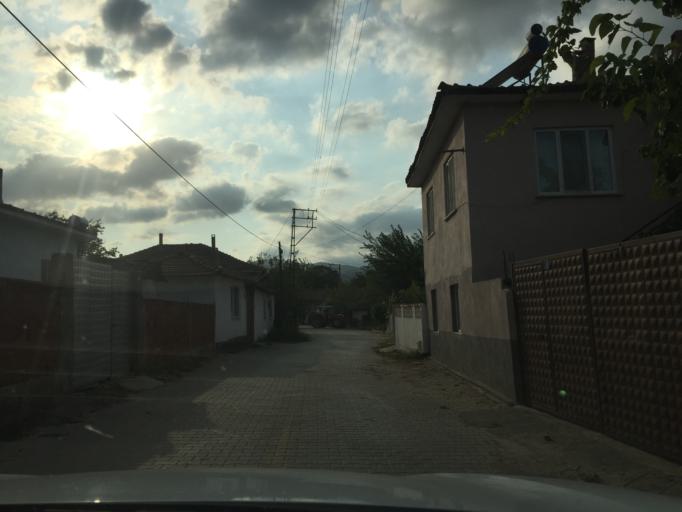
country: TR
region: Balikesir
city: Gonen
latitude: 40.0536
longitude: 27.5931
